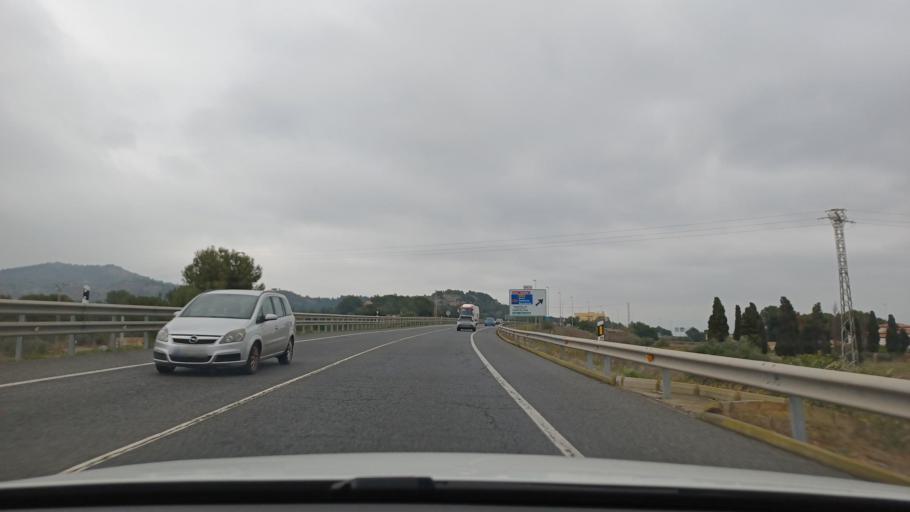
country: ES
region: Valencia
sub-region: Provincia de Castello
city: Borriol
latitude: 40.0016
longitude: -0.0834
